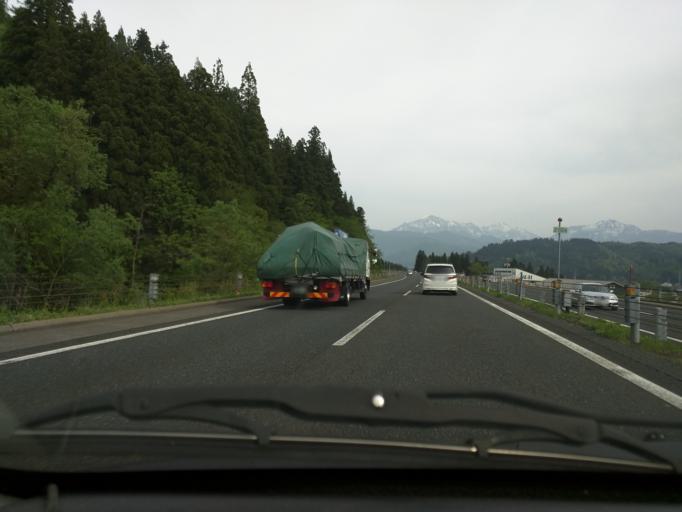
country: JP
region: Niigata
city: Ojiya
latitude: 37.2490
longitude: 138.9362
